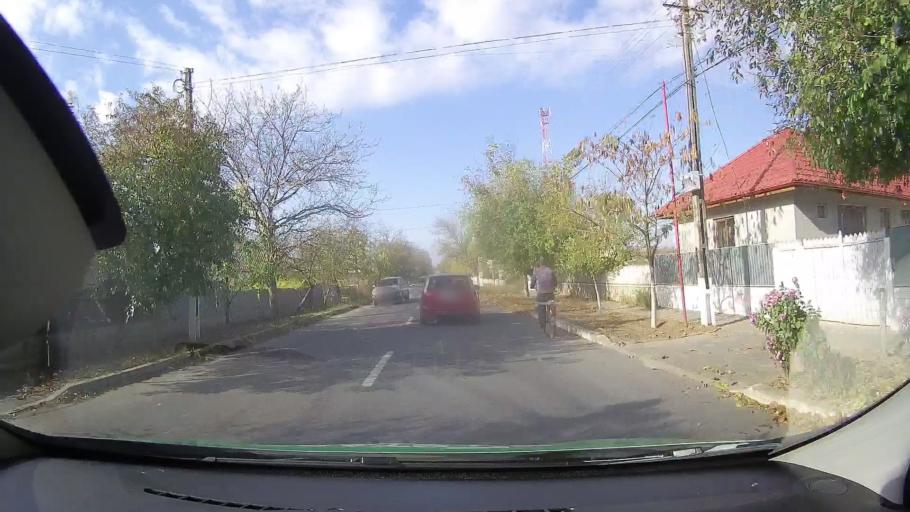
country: RO
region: Tulcea
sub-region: Comuna Sarichioi
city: Sarichioi
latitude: 44.9432
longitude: 28.8511
